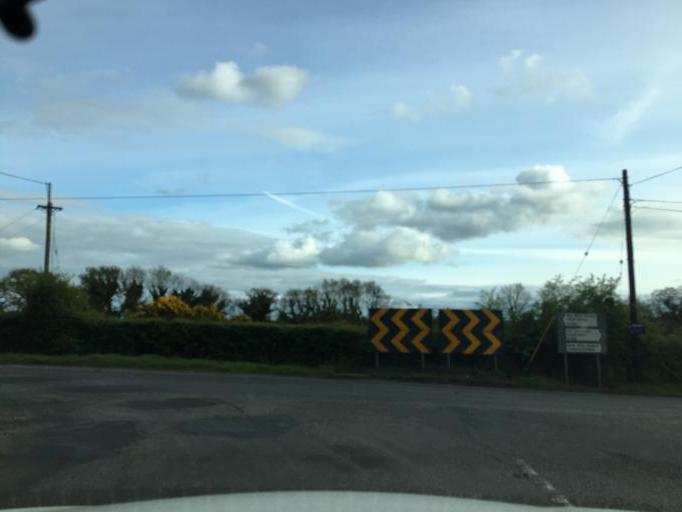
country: IE
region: Leinster
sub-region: Loch Garman
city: New Ross
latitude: 52.4349
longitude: -6.9610
